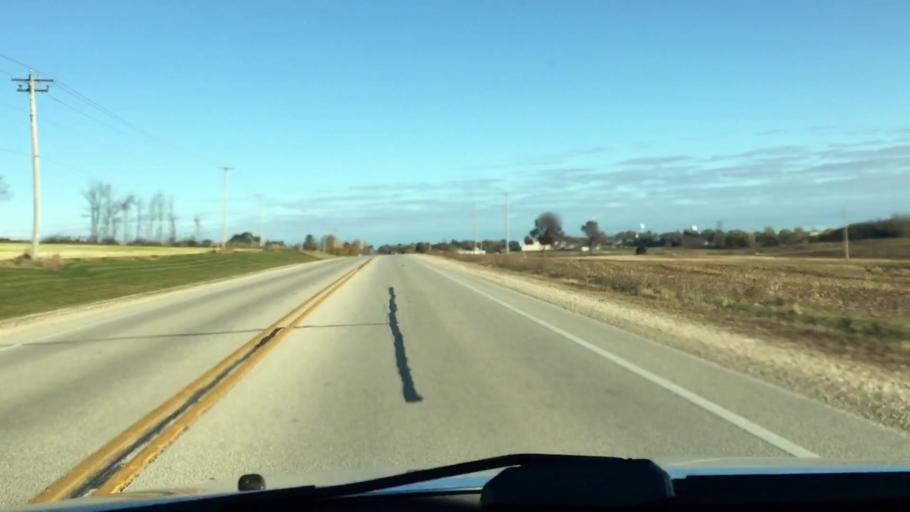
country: US
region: Wisconsin
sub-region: Dodge County
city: Lomira
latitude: 43.5749
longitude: -88.4500
